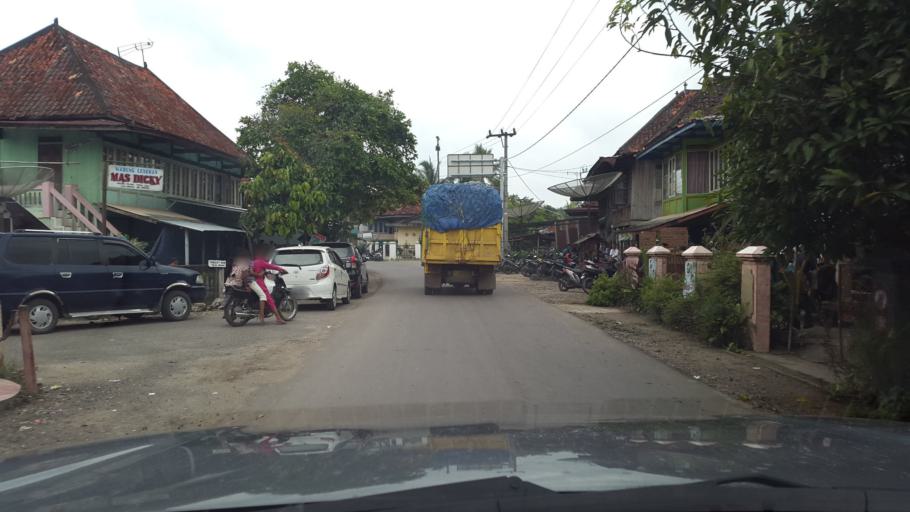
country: ID
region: South Sumatra
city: Gunungmenang
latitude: -3.2207
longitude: 104.0587
